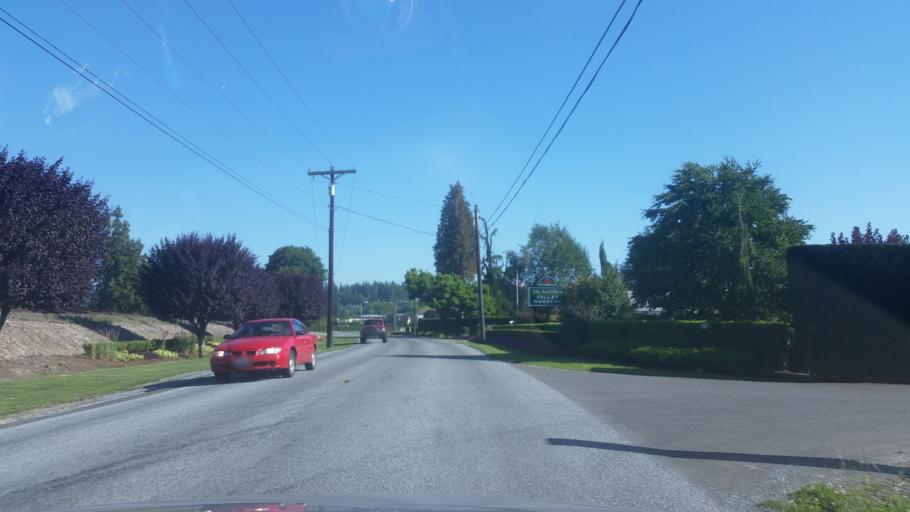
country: US
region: Washington
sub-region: Snohomish County
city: Snohomish
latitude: 47.8890
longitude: -122.0996
